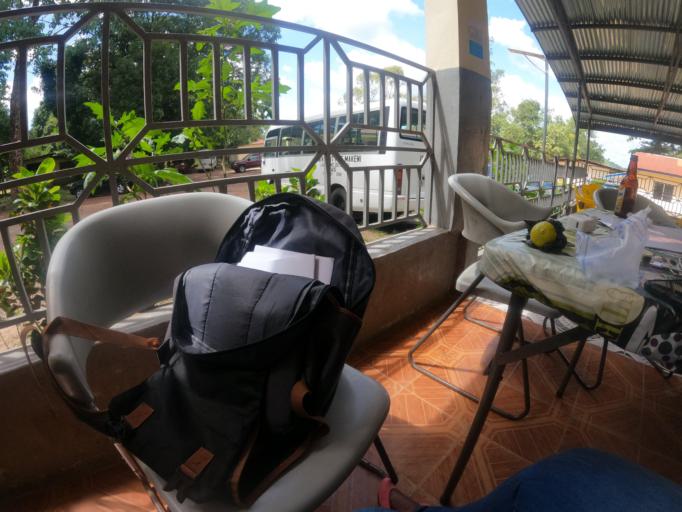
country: SL
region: Northern Province
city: Makeni
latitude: 8.8878
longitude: -12.0578
